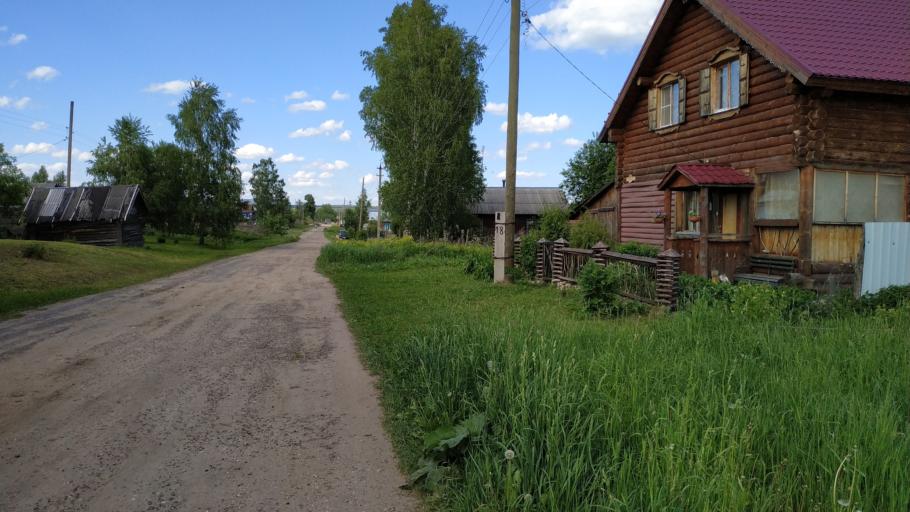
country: RU
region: Nizjnij Novgorod
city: Bogorodsk
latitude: 55.8835
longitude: 43.5563
